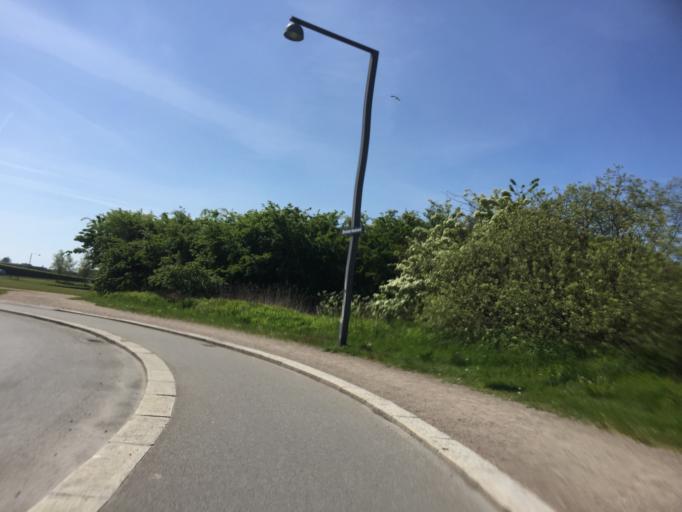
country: DK
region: Capital Region
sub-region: Kobenhavn
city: Christianshavn
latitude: 55.6550
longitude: 12.5884
